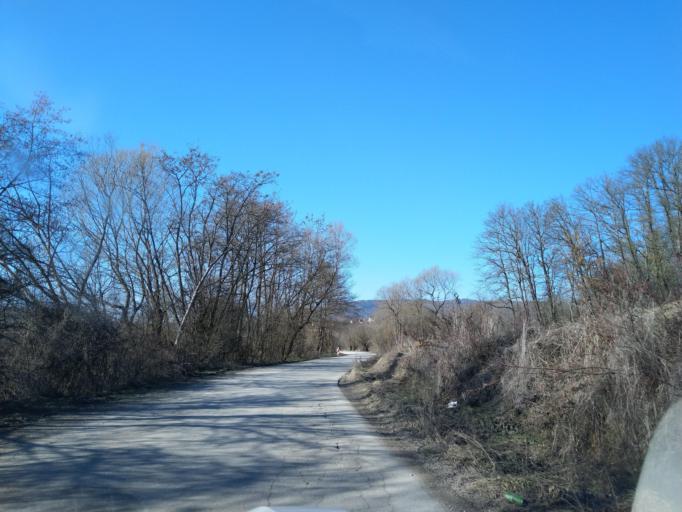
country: RS
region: Central Serbia
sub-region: Zlatiborski Okrug
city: Kosjeric
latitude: 43.9329
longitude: 19.8881
